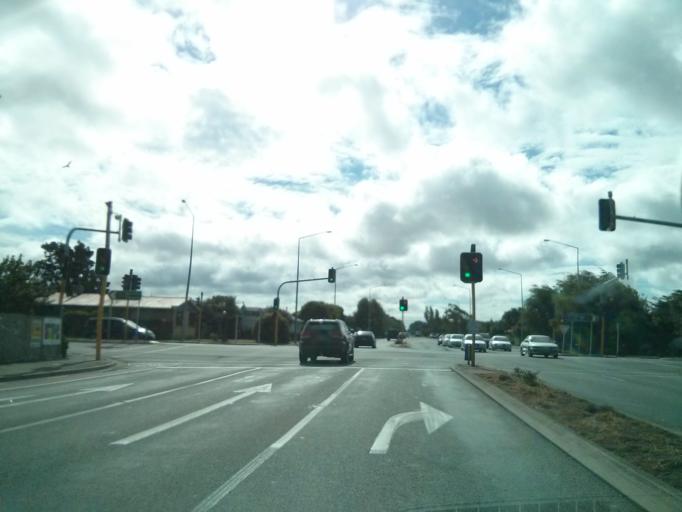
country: NZ
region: Canterbury
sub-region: Selwyn District
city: Prebbleton
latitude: -43.5205
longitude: 172.5346
